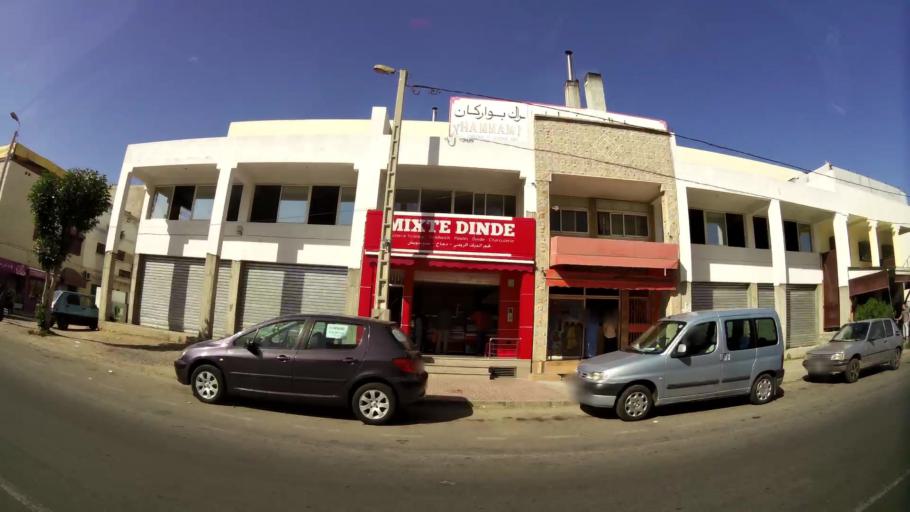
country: MA
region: Oued ed Dahab-Lagouira
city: Dakhla
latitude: 30.4245
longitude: -9.5651
